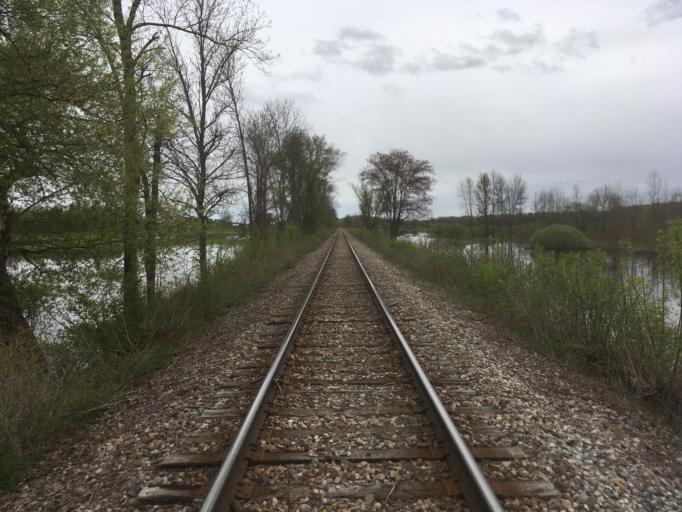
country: US
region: Vermont
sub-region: Addison County
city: Middlebury (village)
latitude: 43.9571
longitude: -73.1623
